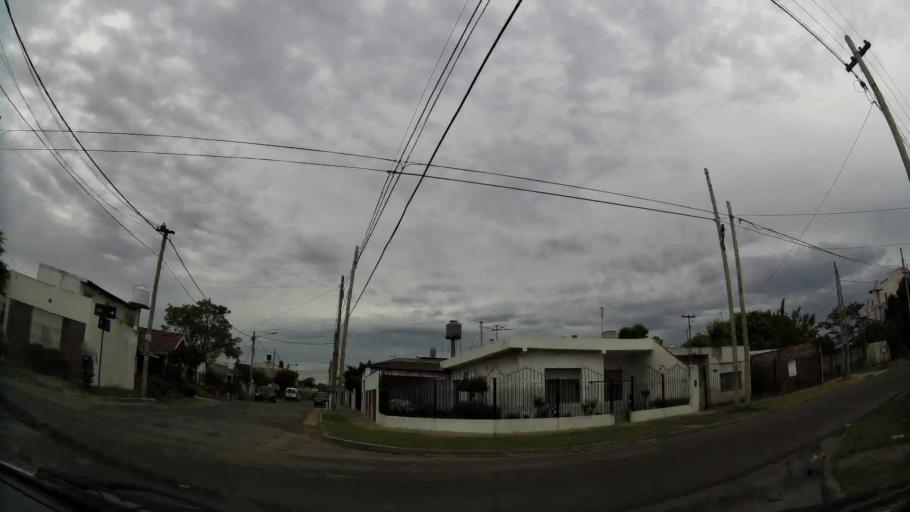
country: AR
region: Buenos Aires
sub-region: Partido de Quilmes
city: Quilmes
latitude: -34.7630
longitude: -58.1961
